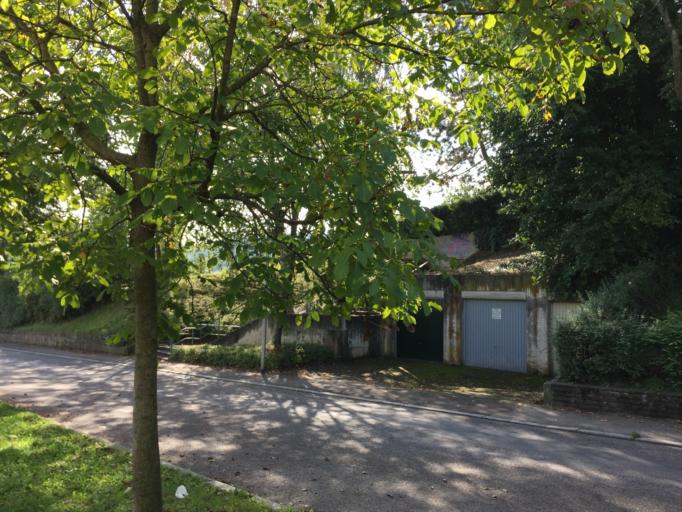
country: DE
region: Baden-Wuerttemberg
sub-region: Regierungsbezirk Stuttgart
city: Heilbronn
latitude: 49.1334
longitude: 9.2468
